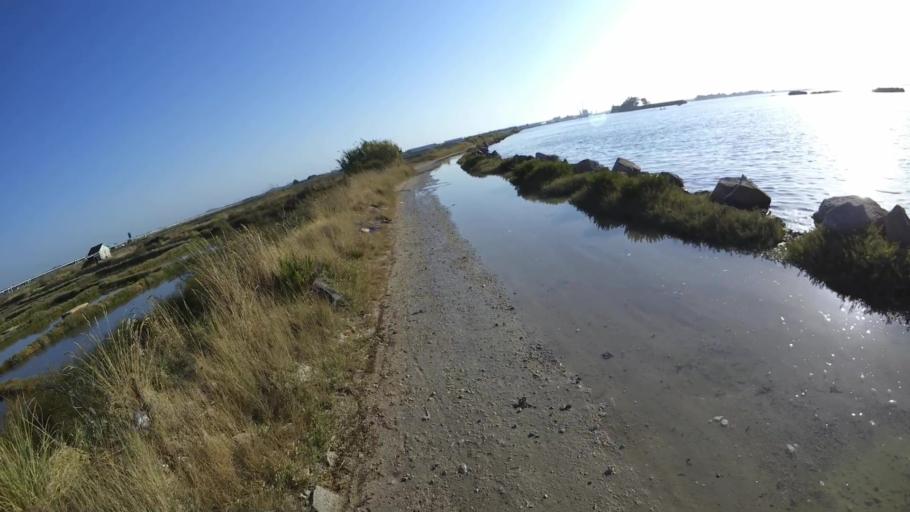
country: PT
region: Aveiro
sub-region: Aveiro
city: Aveiro
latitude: 40.6440
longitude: -8.6654
